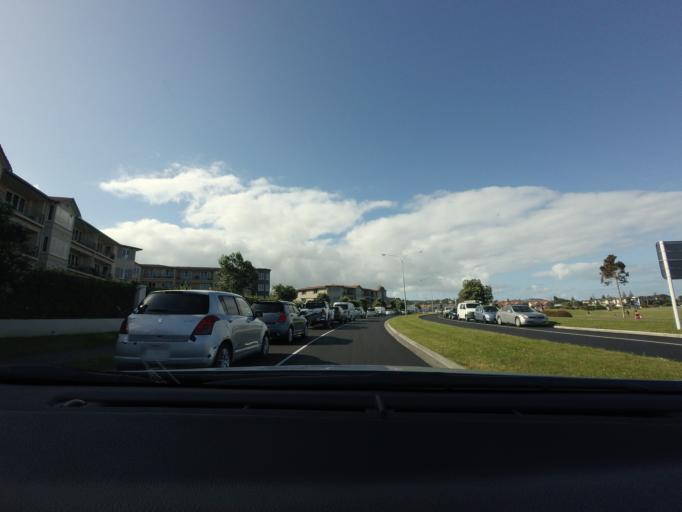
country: NZ
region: Auckland
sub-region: Auckland
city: Rothesay Bay
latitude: -36.5839
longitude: 174.6857
